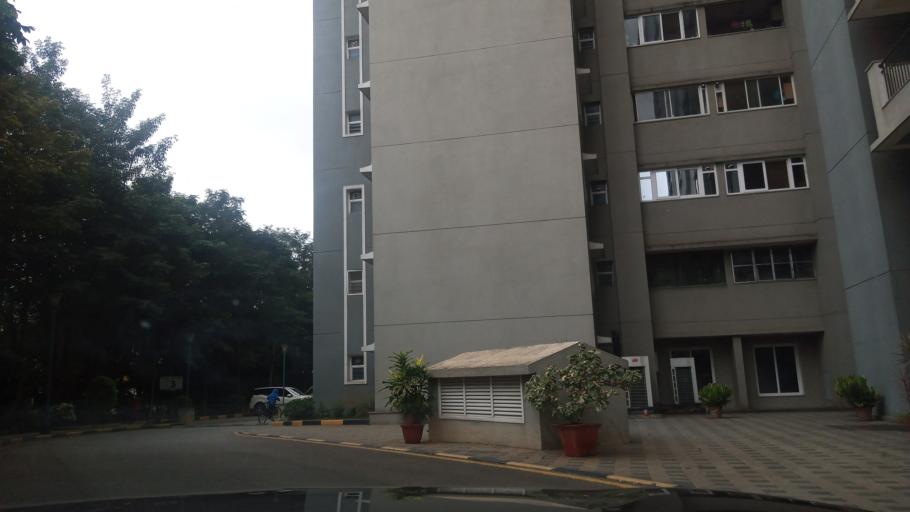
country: IN
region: Karnataka
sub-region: Bangalore Urban
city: Yelahanka
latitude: 13.0445
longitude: 77.4999
